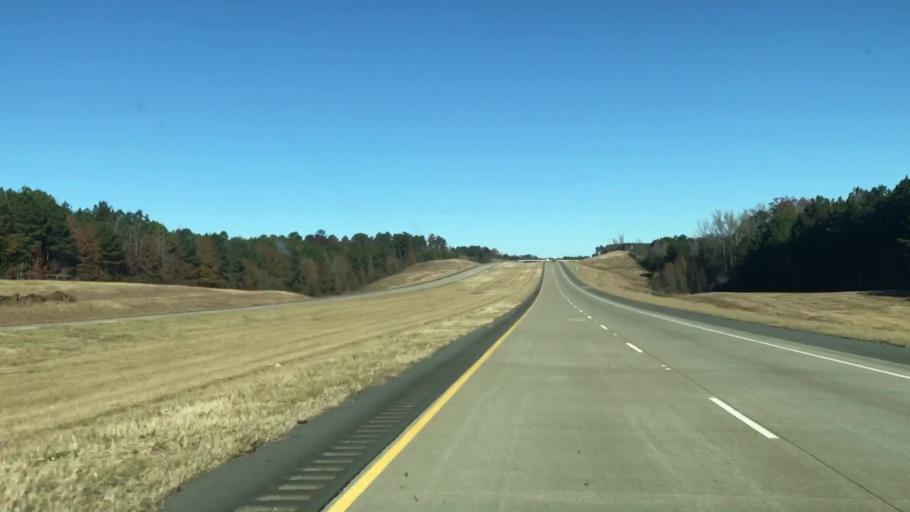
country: US
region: Louisiana
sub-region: Caddo Parish
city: Vivian
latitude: 32.9647
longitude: -93.9046
